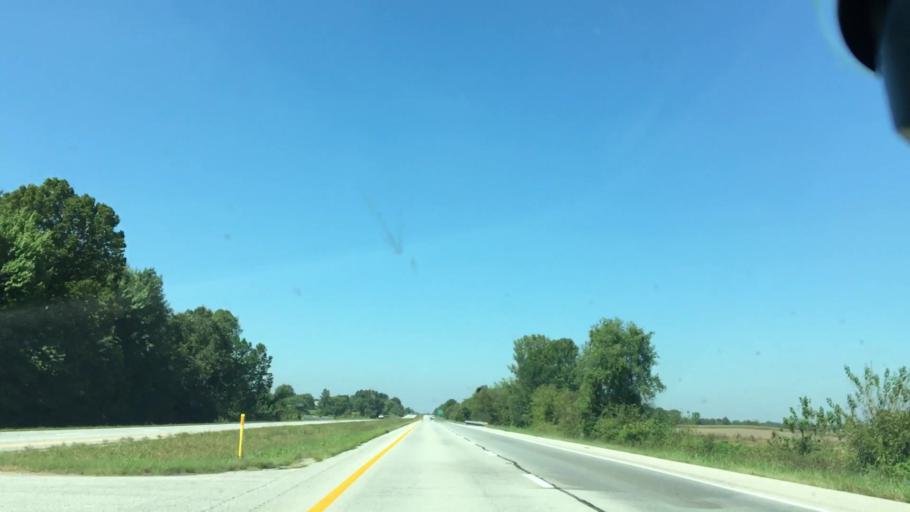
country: US
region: Kentucky
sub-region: Henderson County
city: Henderson
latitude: 37.7647
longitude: -87.5329
